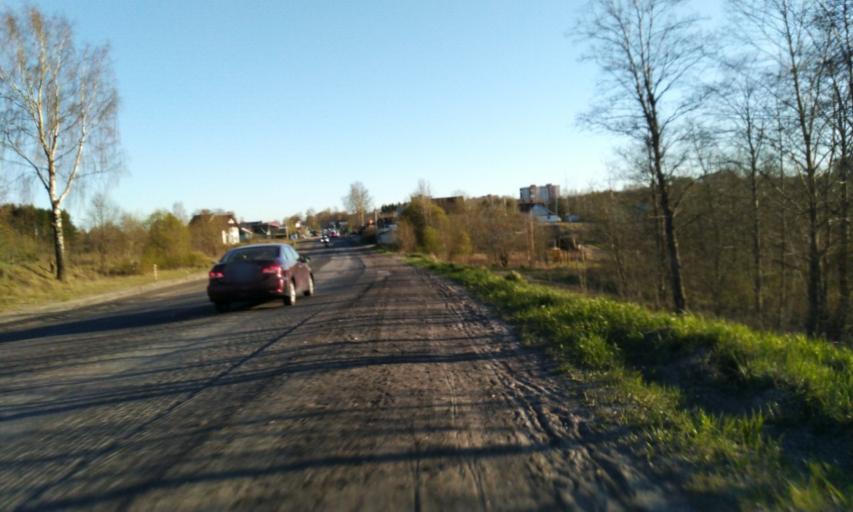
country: RU
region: Leningrad
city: Toksovo
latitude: 60.1164
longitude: 30.5039
